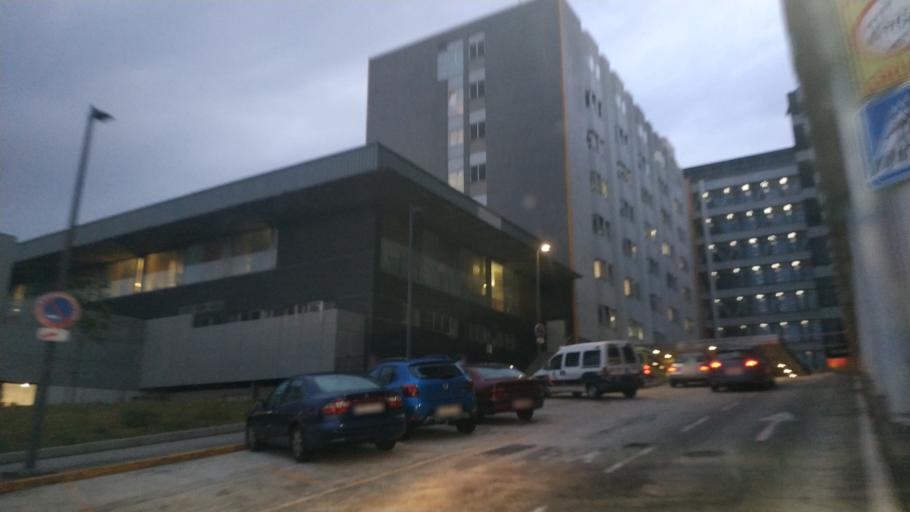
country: ES
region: Galicia
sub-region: Provincia da Coruna
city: A Coruna
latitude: 43.3448
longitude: -8.3888
